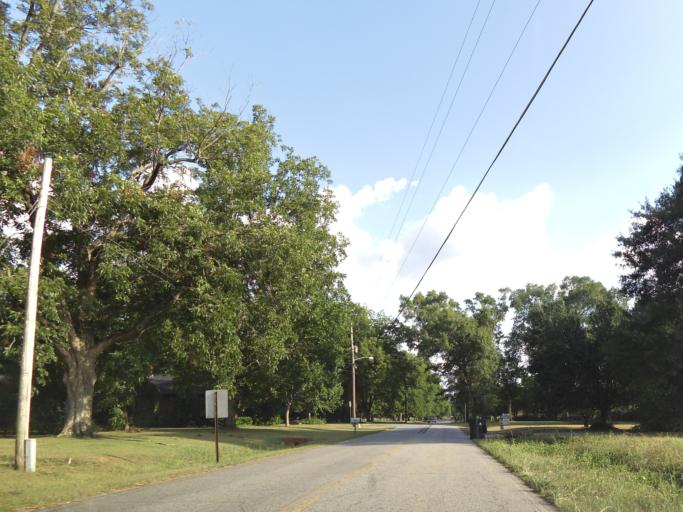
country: US
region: Georgia
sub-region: Houston County
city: Centerville
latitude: 32.7092
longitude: -83.6792
